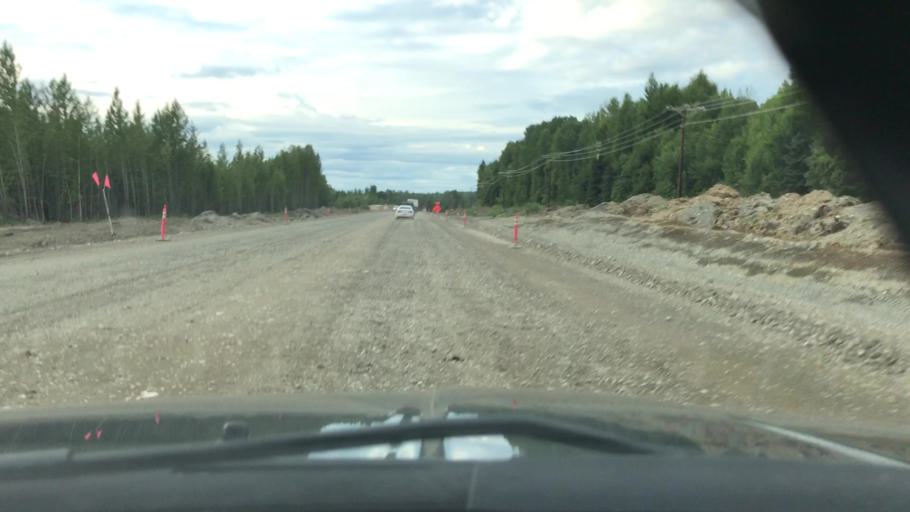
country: US
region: Alaska
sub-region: Matanuska-Susitna Borough
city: Y
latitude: 62.0915
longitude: -150.0615
